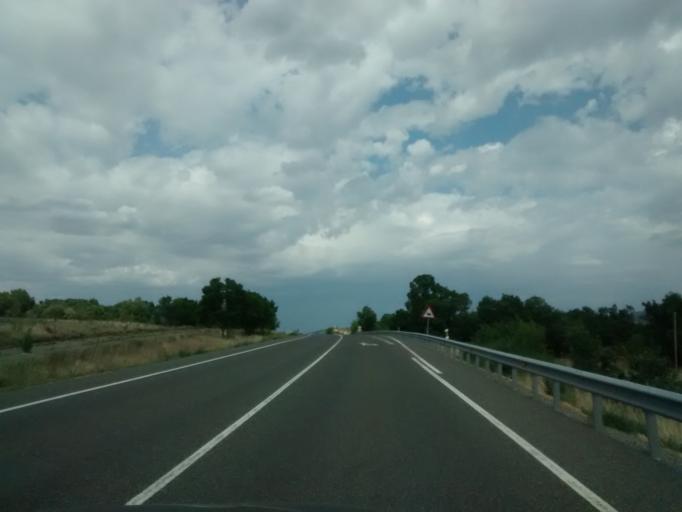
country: ES
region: Castille and Leon
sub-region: Provincia de Segovia
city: Navafria
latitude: 41.0675
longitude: -3.8173
